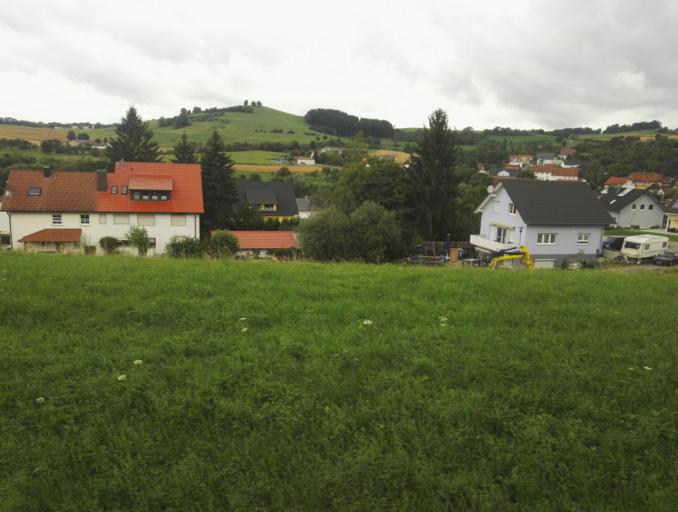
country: DE
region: Baden-Wuerttemberg
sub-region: Freiburg Region
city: Blumberg
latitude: 47.8039
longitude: 8.5318
